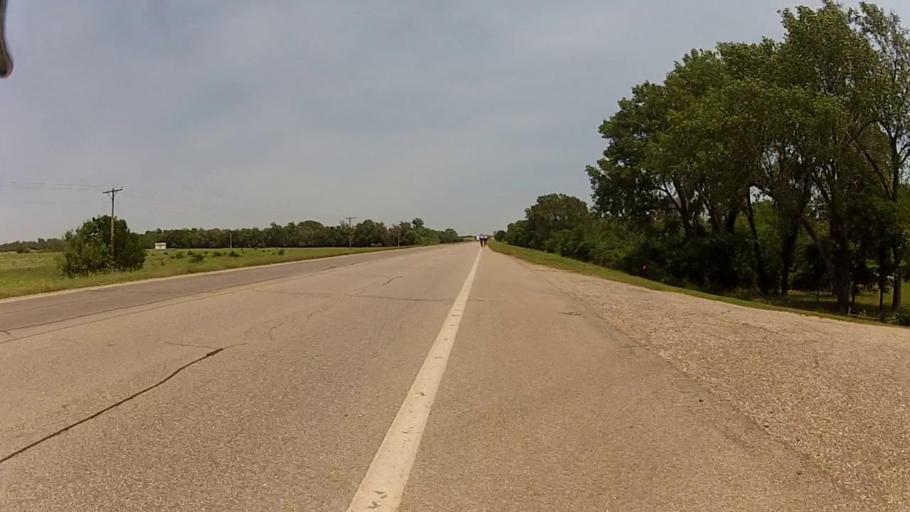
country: US
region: Kansas
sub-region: Cowley County
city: Arkansas City
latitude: 37.0564
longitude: -97.0668
